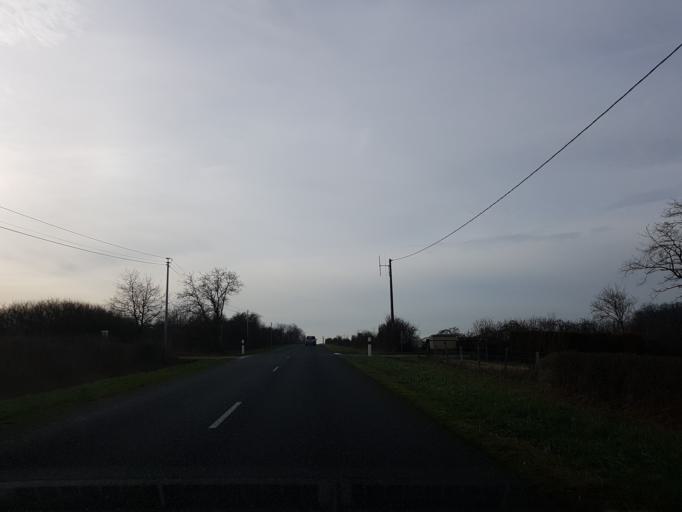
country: FR
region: Auvergne
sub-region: Departement de l'Allier
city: Lusigny
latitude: 46.6186
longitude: 3.5702
